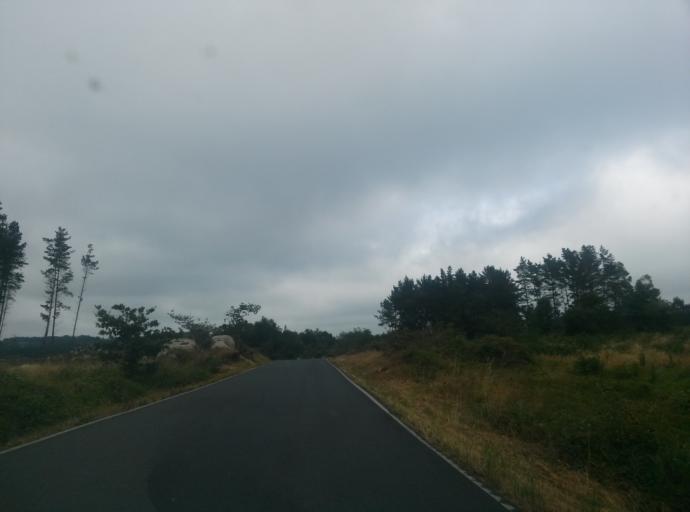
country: ES
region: Galicia
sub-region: Provincia de Lugo
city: Lugo
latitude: 43.0740
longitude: -7.5521
